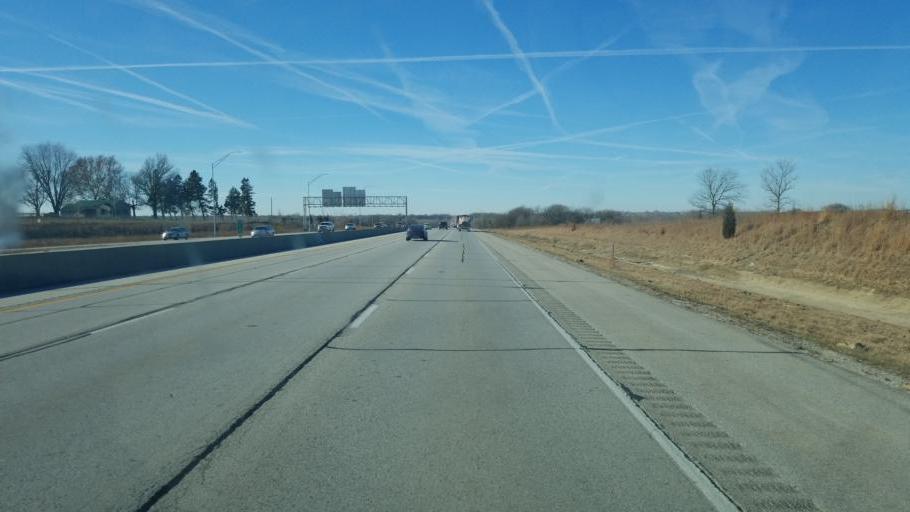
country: US
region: Iowa
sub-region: Polk County
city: Altoona
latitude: 41.6596
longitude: -93.5258
